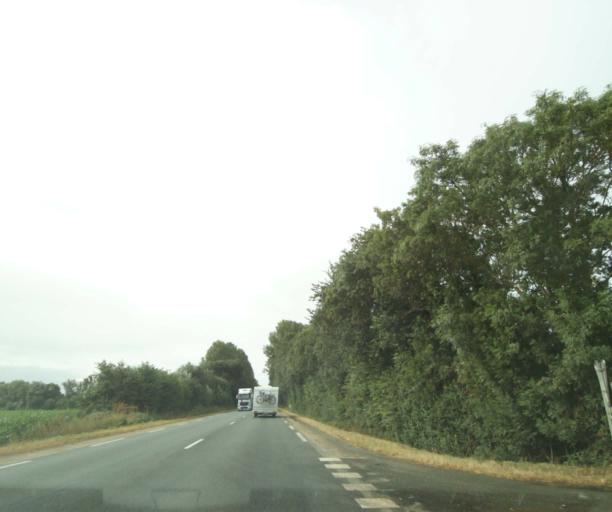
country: FR
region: Pays de la Loire
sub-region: Departement de la Vendee
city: Sainte-Gemme-la-Plaine
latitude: 46.4476
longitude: -1.1029
